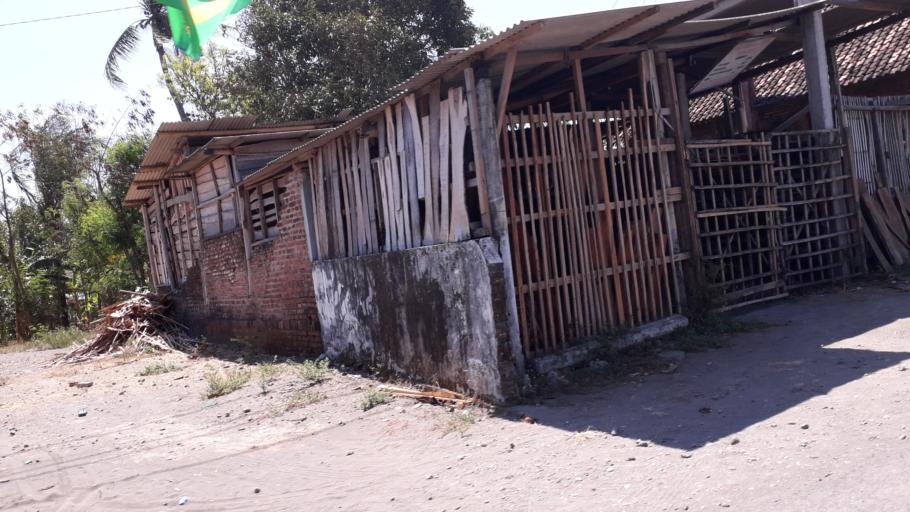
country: ID
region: Daerah Istimewa Yogyakarta
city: Pundong
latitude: -7.9913
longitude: 110.3154
